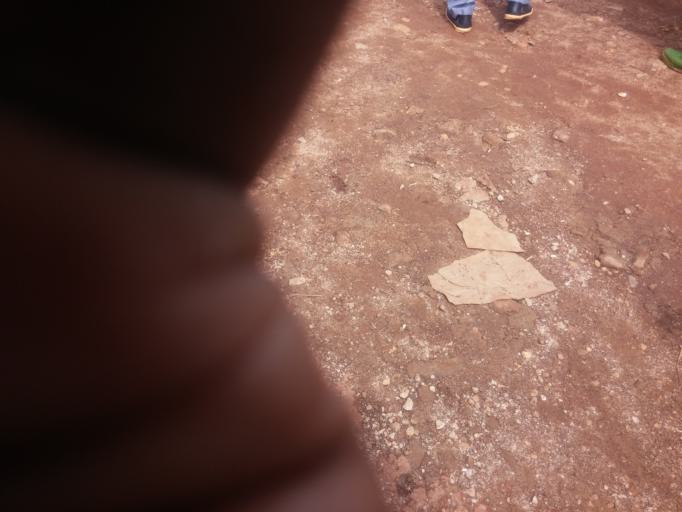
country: TG
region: Centrale
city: Sotouboua
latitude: 8.5587
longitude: 0.9743
